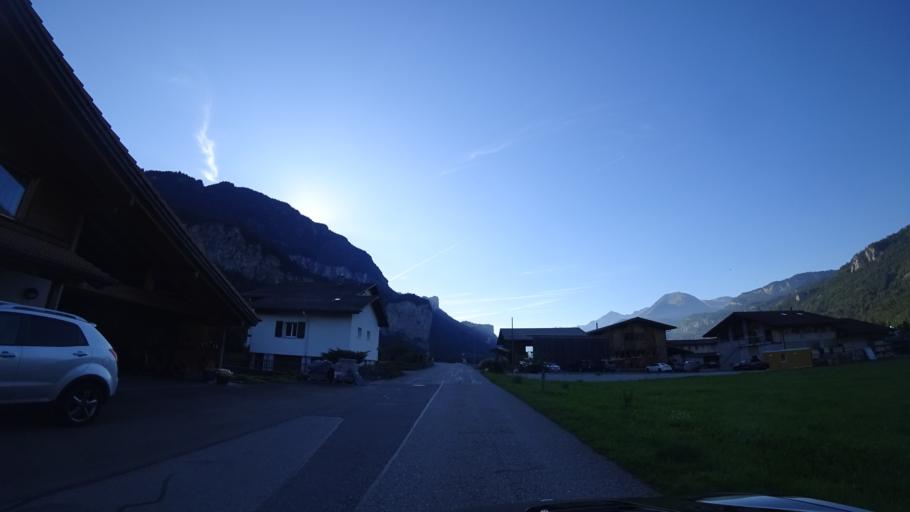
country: CH
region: Bern
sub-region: Interlaken-Oberhasli District
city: Meiringen
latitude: 46.7209
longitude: 8.1912
